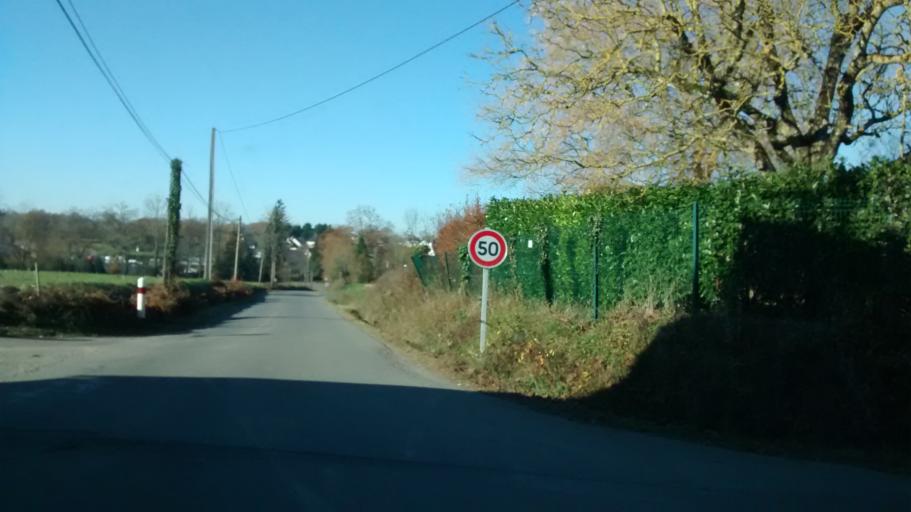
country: FR
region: Brittany
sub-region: Departement d'Ille-et-Vilaine
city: Liffre
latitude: 48.2034
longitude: -1.5055
